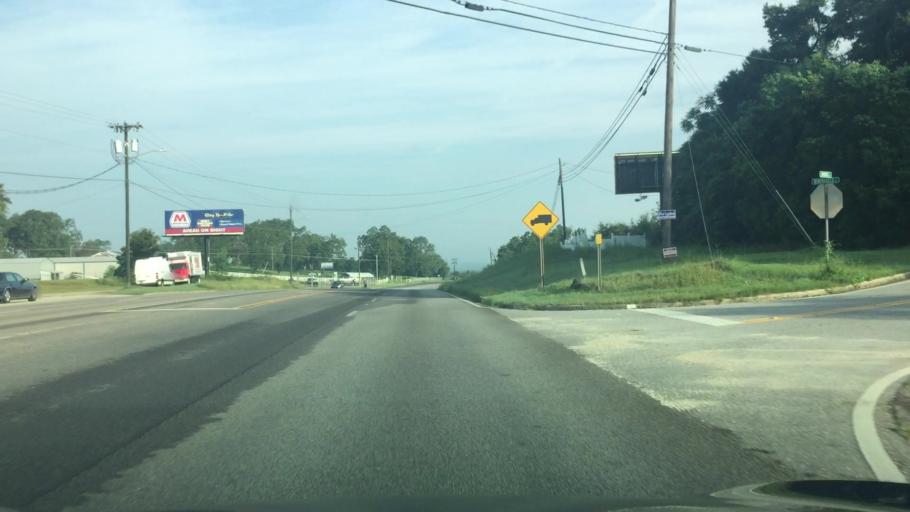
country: US
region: Alabama
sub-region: Covington County
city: Andalusia
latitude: 31.3242
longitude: -86.5074
